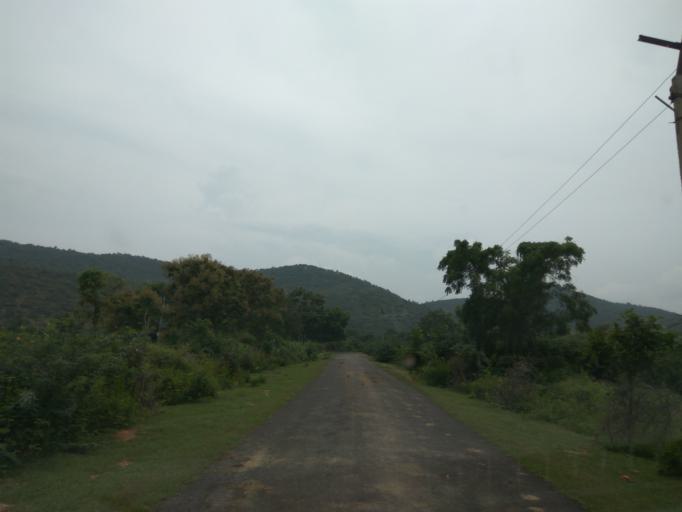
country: IN
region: Andhra Pradesh
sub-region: Prakasam
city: Cumbum
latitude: 15.4470
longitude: 79.0798
